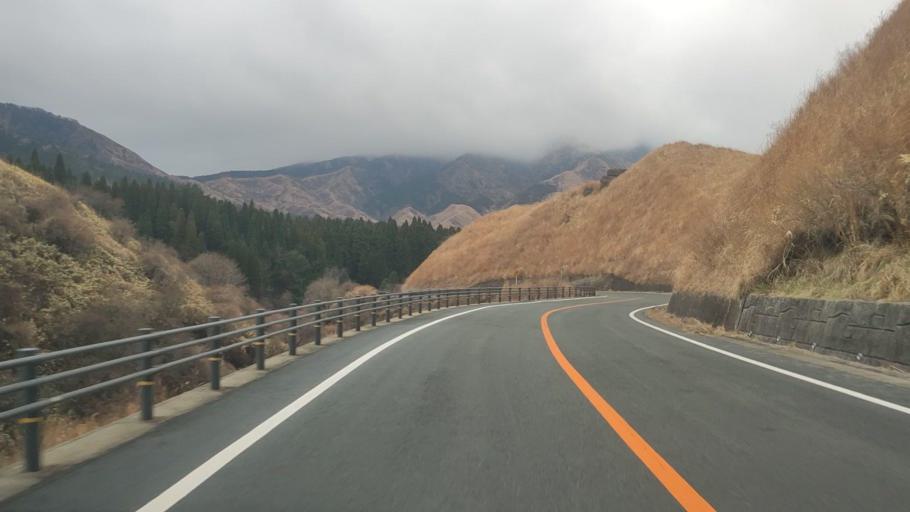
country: JP
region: Kumamoto
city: Aso
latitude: 32.9053
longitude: 131.1467
